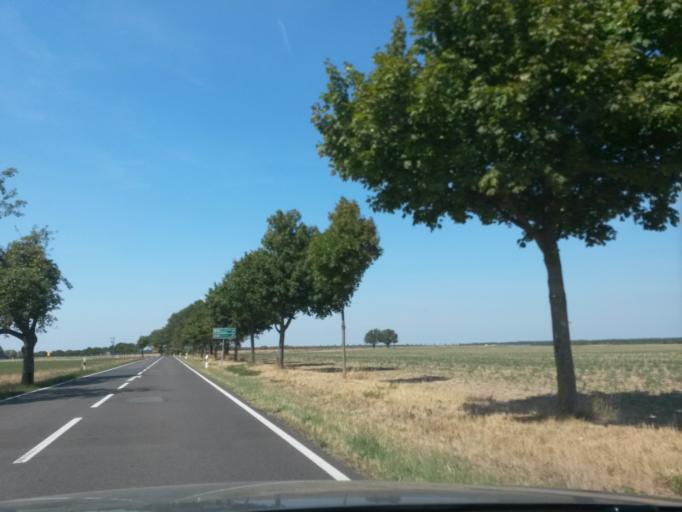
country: DE
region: Brandenburg
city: Wiesenburg
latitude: 52.1642
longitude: 12.4816
